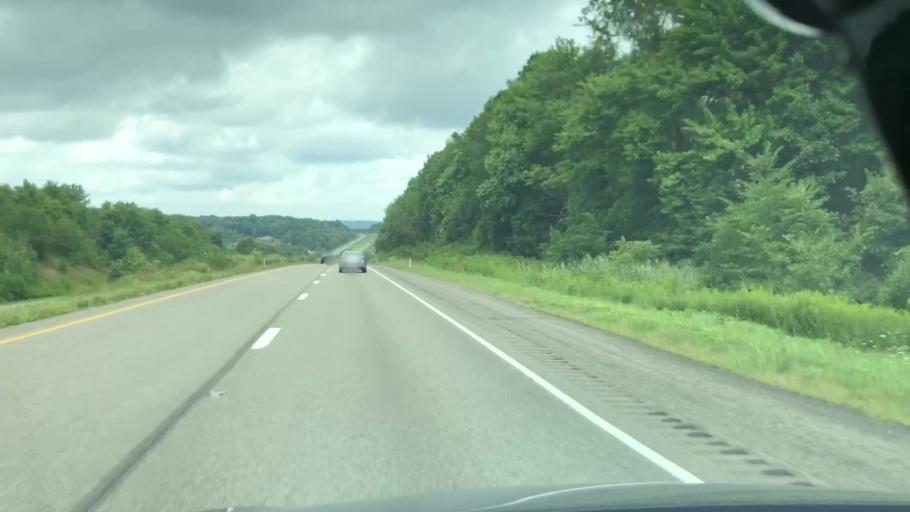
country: US
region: Pennsylvania
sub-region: Crawford County
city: Meadville
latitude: 41.5817
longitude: -80.1759
